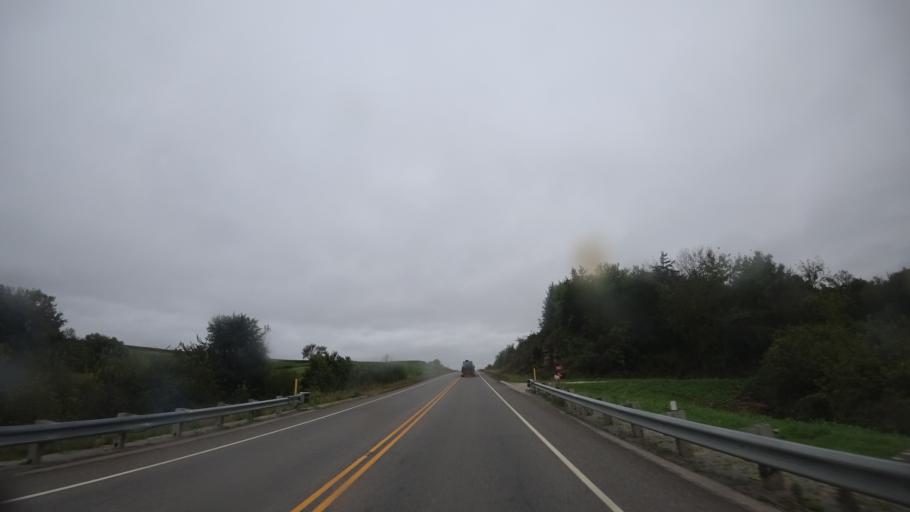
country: US
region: Wisconsin
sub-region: Crawford County
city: Prairie du Chien
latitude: 43.0227
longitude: -91.0297
